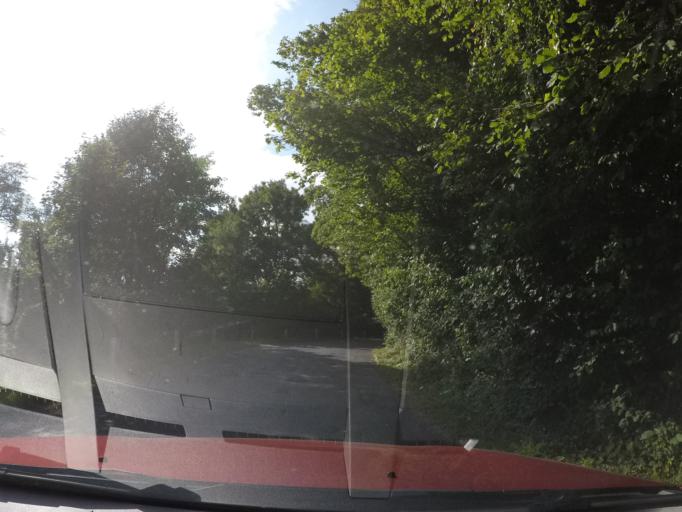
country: UA
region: Zakarpattia
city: Velykyi Bereznyi
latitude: 48.9161
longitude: 22.4588
